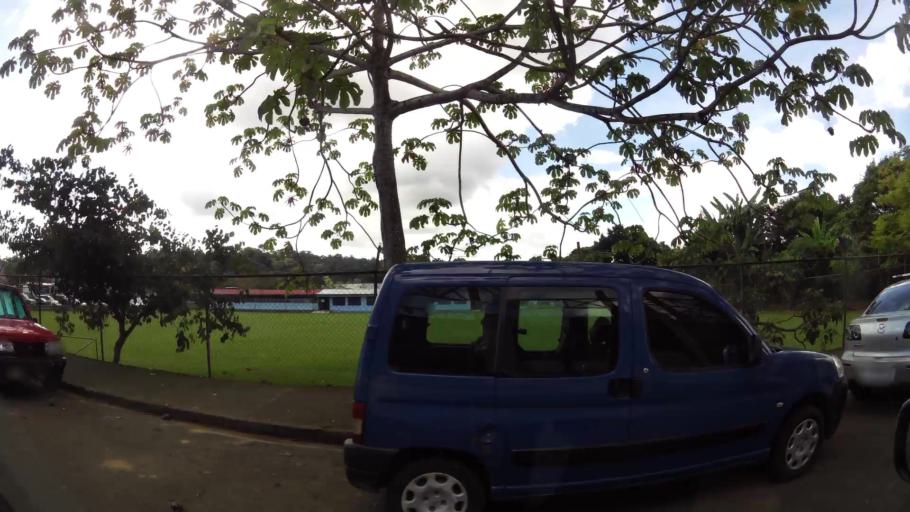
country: CR
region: San Jose
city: San Isidro
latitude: 9.3683
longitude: -83.7049
